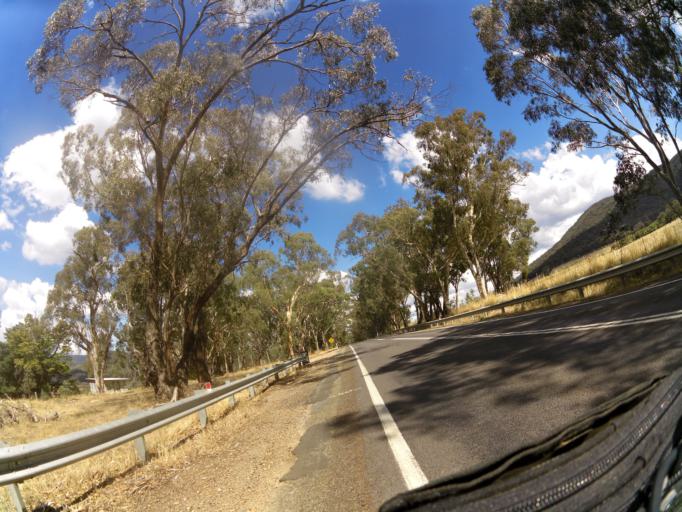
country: AU
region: Victoria
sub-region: Mansfield
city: Mansfield
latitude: -36.8088
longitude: 146.0070
